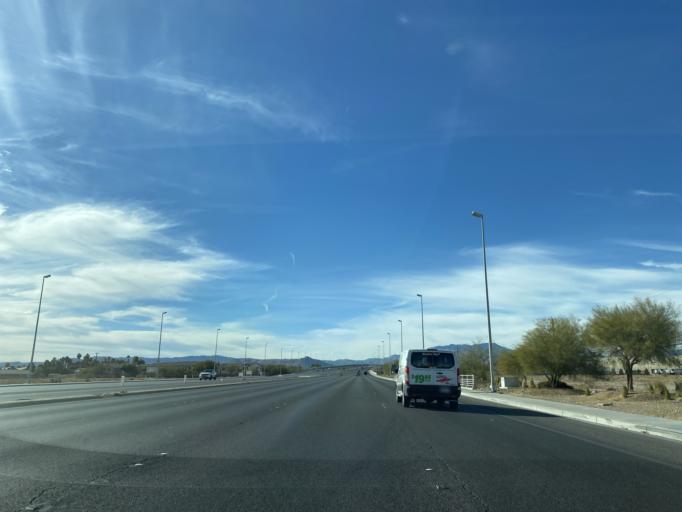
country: US
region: Nevada
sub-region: Clark County
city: Enterprise
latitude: 36.0286
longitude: -115.2167
